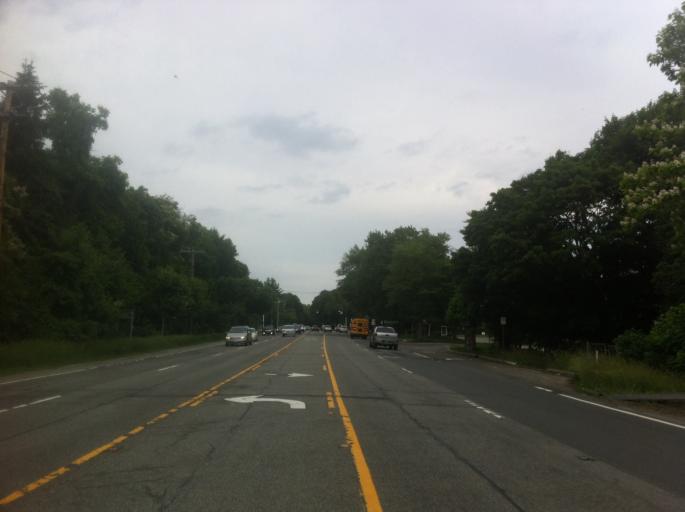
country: US
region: New York
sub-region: Nassau County
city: Old Brookville
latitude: 40.8237
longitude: -73.5919
